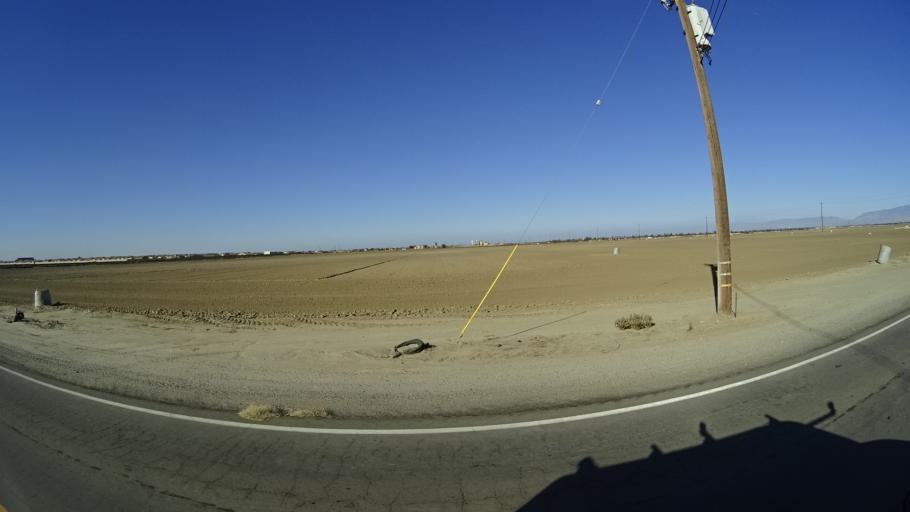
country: US
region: California
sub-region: Kern County
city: Greenfield
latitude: 35.2816
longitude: -119.0990
